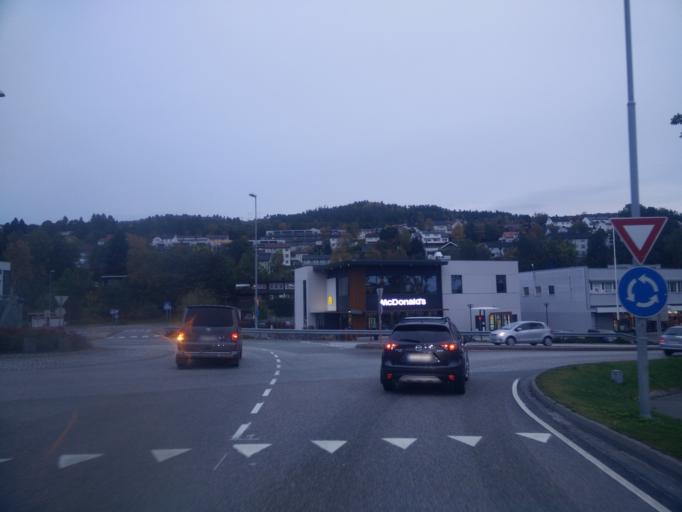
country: NO
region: More og Romsdal
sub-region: Molde
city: Molde
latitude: 62.7385
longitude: 7.1817
